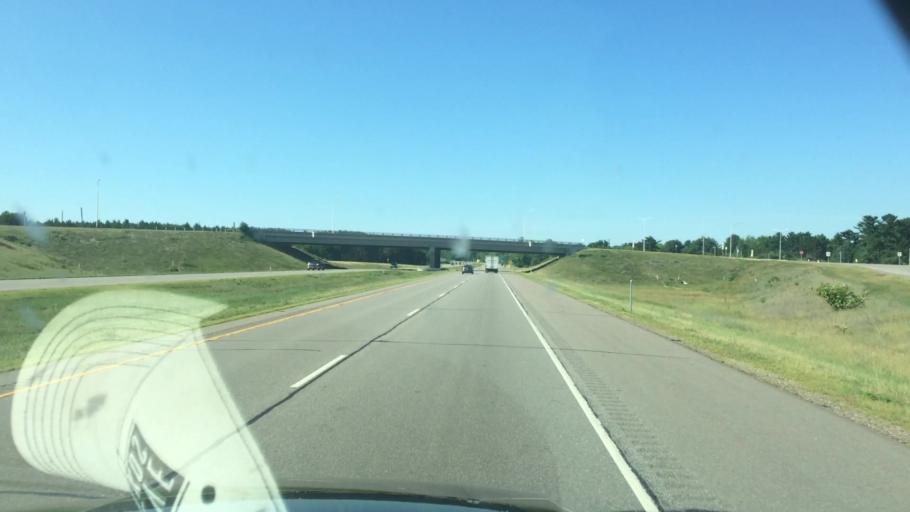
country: US
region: Wisconsin
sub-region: Marathon County
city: Mosinee
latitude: 44.8132
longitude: -89.6711
